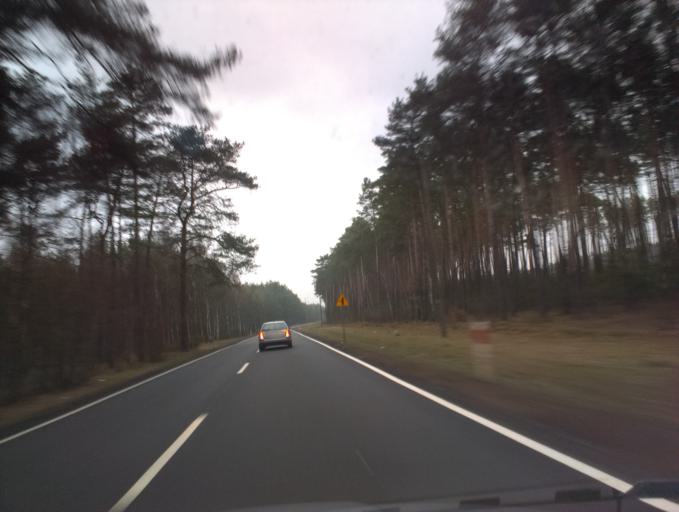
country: PL
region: Greater Poland Voivodeship
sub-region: Powiat zlotowski
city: Tarnowka
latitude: 53.3438
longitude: 16.7905
